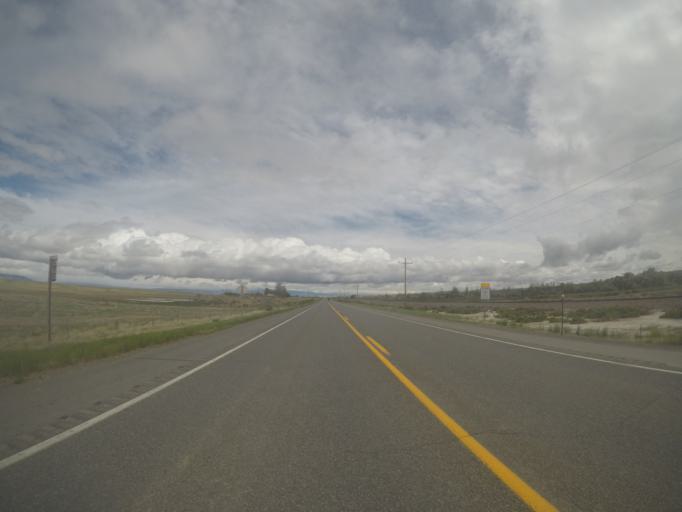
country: US
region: Wyoming
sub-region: Big Horn County
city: Lovell
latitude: 44.8920
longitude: -108.5881
